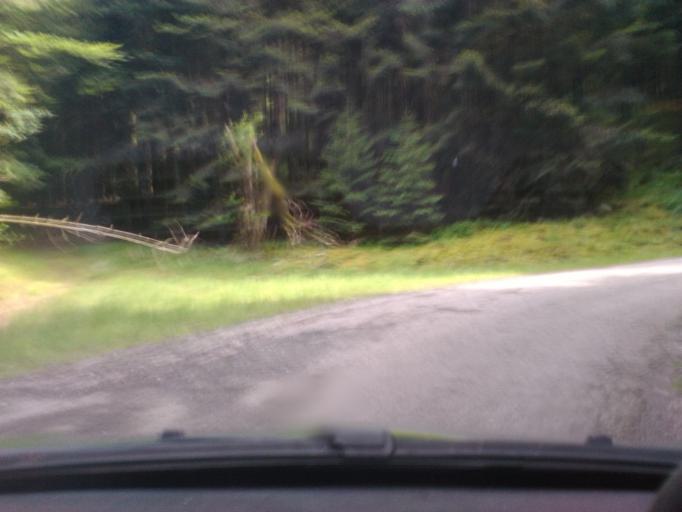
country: FR
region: Lorraine
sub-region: Departement des Vosges
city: Granges-sur-Vologne
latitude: 48.2228
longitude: 6.8110
